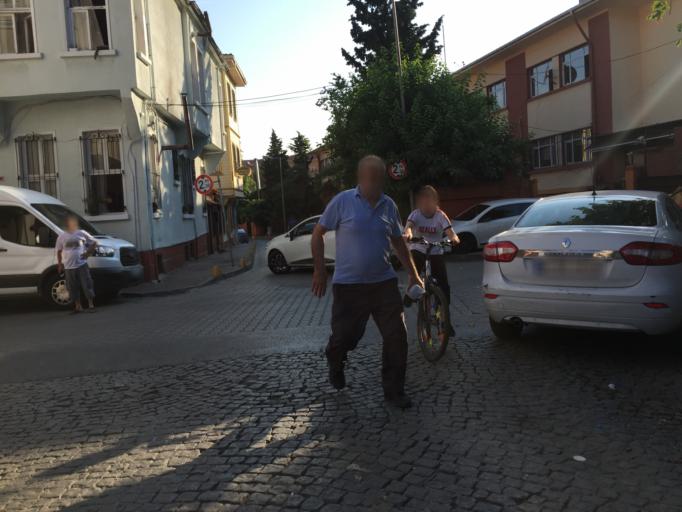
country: TR
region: Istanbul
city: Eminoenue
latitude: 41.0041
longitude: 28.9690
